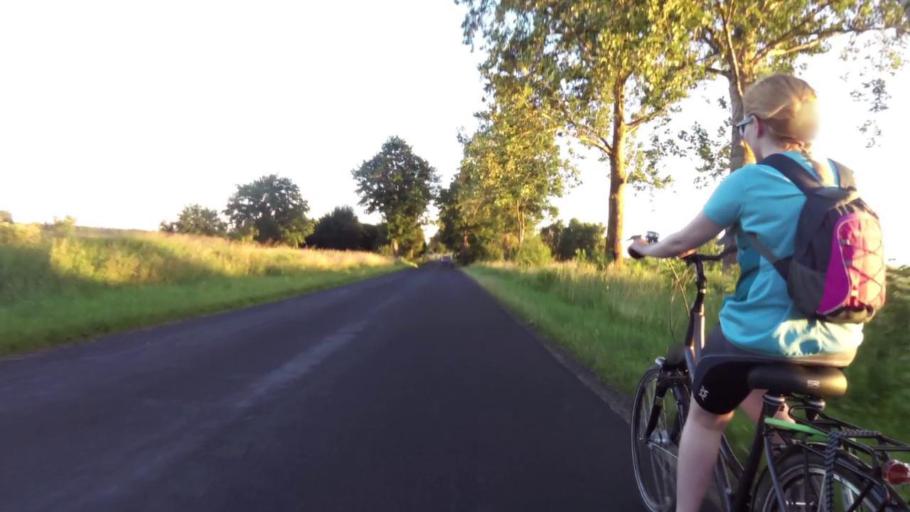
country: PL
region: West Pomeranian Voivodeship
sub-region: Powiat bialogardzki
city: Bialogard
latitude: 54.0209
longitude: 16.0121
